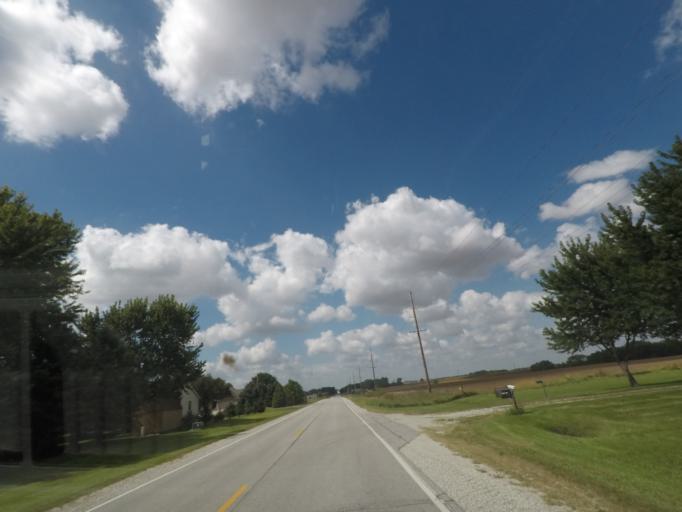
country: US
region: Iowa
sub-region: Story County
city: Nevada
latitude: 42.0225
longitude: -93.3226
